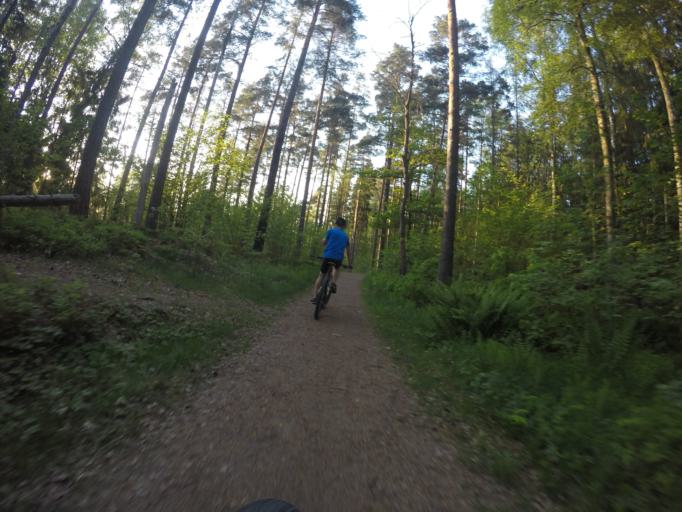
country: SE
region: Soedermanland
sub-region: Eskilstuna Kommun
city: Skogstorp
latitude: 59.3381
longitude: 16.4956
